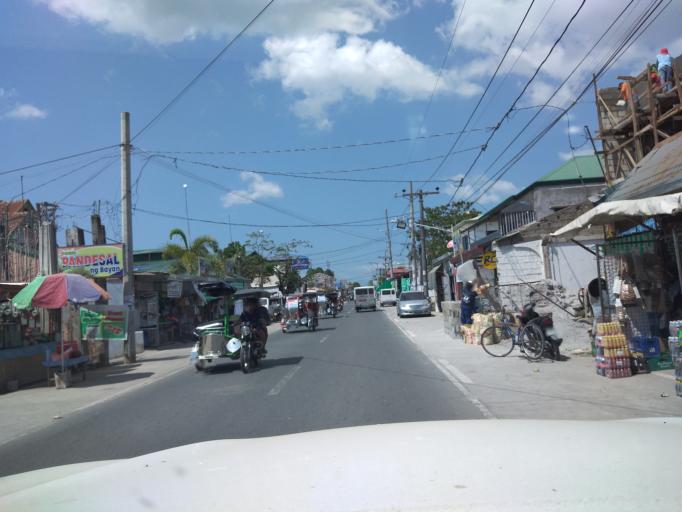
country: PH
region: Central Luzon
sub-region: Province of Pampanga
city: Bahay Pare
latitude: 15.0270
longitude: 120.8825
